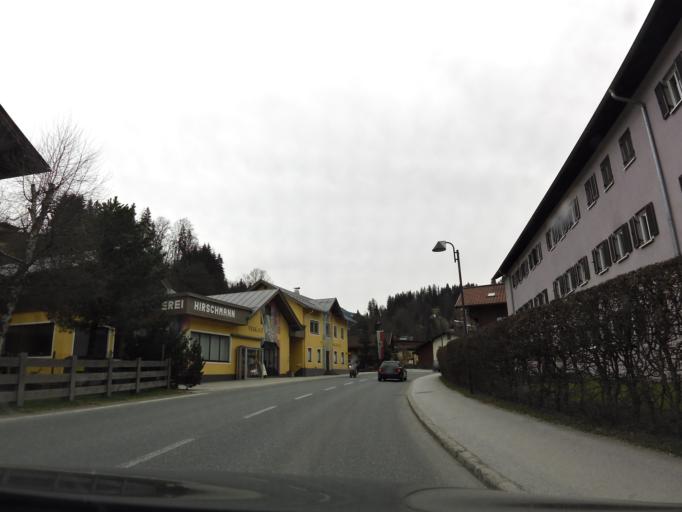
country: AT
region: Tyrol
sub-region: Politischer Bezirk Kitzbuhel
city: Hopfgarten im Brixental
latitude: 47.4408
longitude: 12.1641
